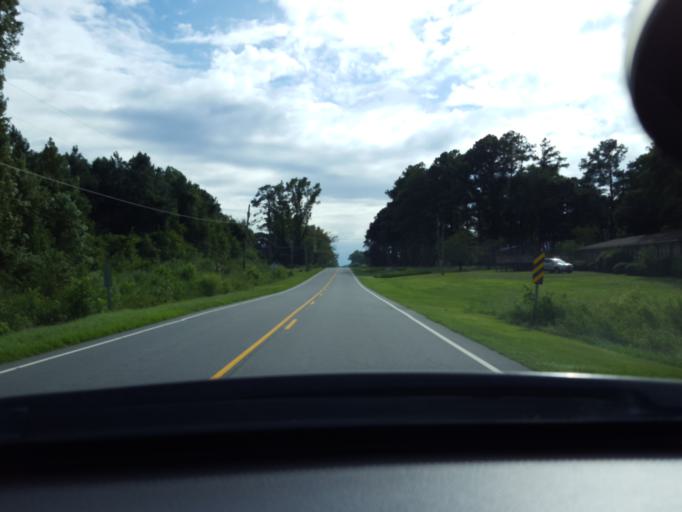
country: US
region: North Carolina
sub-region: Duplin County
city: Kenansville
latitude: 35.0057
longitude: -77.9101
